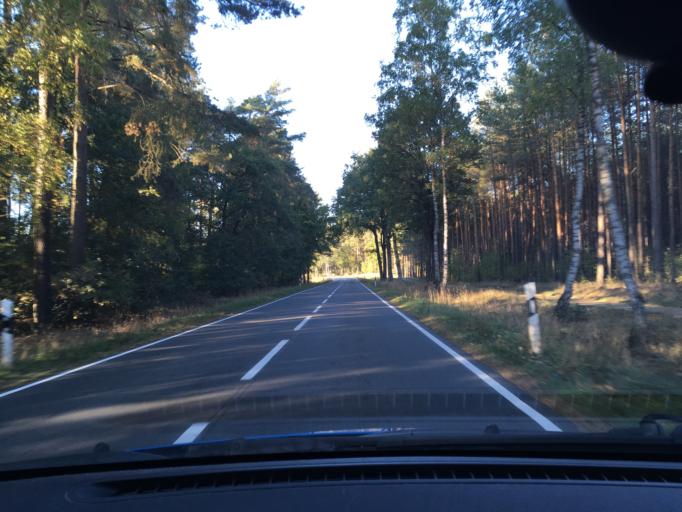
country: DE
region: Lower Saxony
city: Neu Darchau
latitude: 53.2628
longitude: 10.9564
